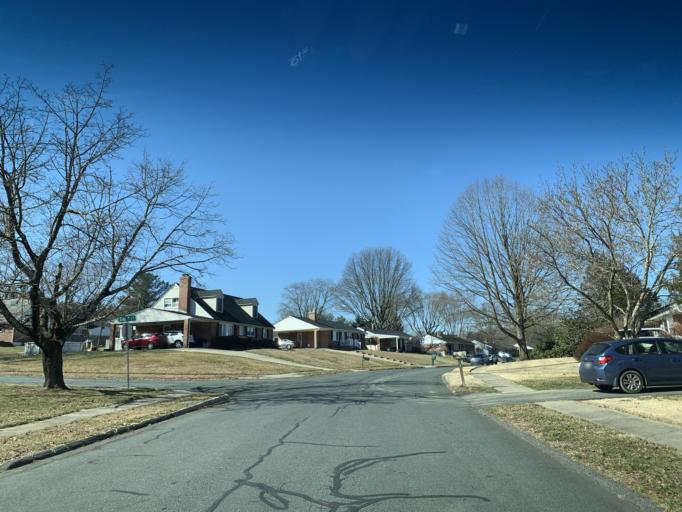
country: US
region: Maryland
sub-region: Harford County
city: Bel Air South
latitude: 39.5359
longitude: -76.2966
